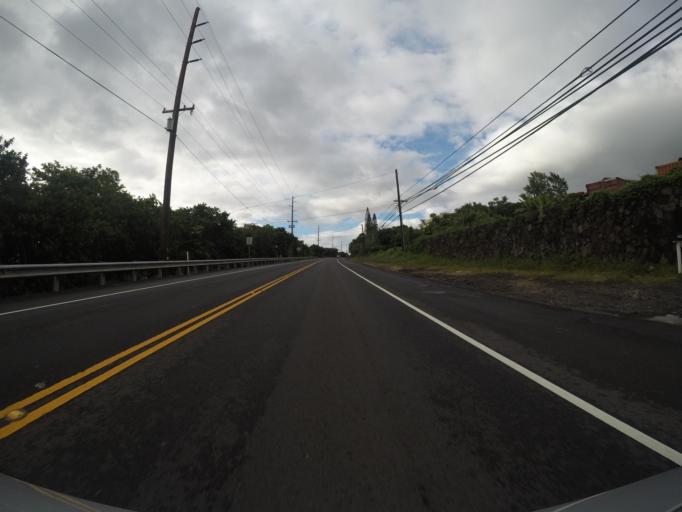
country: US
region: Hawaii
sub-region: Hawaii County
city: Kalaoa
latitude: 19.7287
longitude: -155.9794
